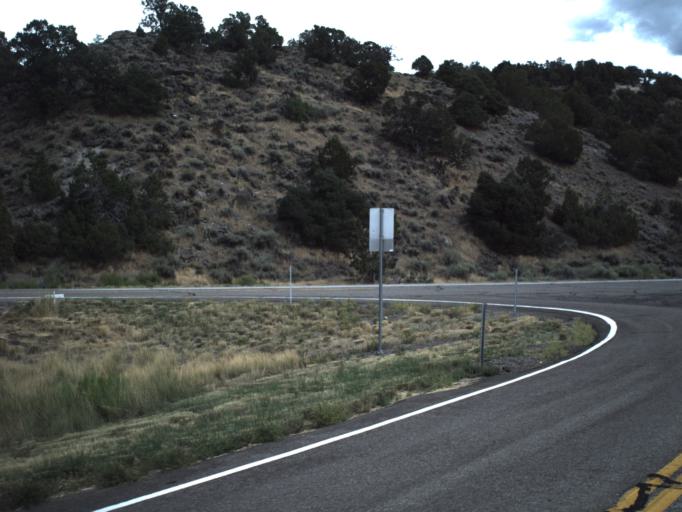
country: US
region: Utah
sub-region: Sevier County
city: Aurora
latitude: 38.7703
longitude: -111.9283
